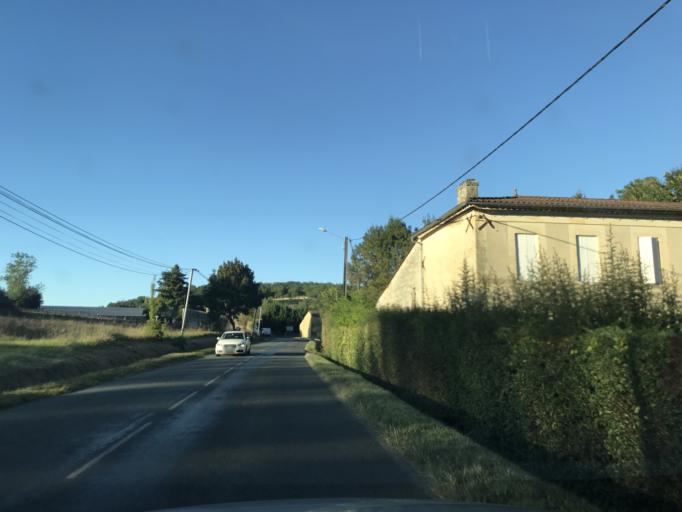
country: FR
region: Aquitaine
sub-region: Departement de la Gironde
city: Mouliets-et-Villemartin
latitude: 44.8727
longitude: -0.0485
